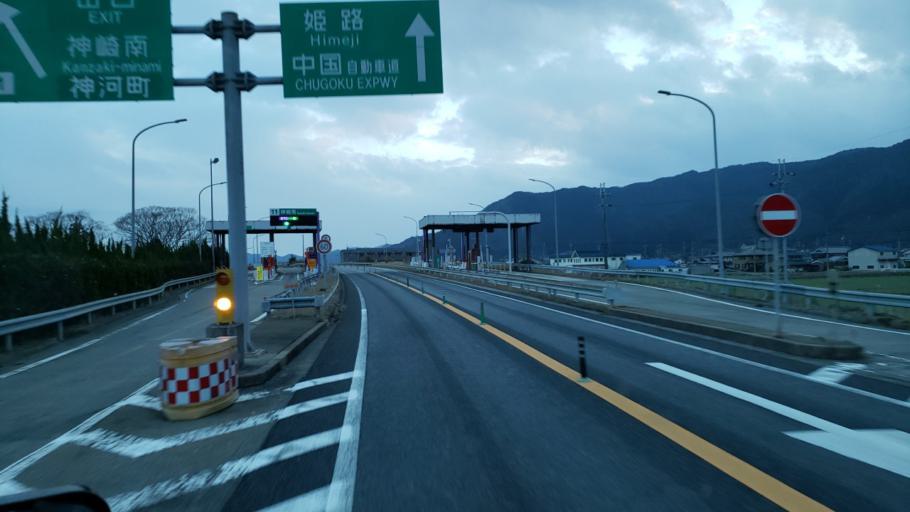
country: JP
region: Hyogo
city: Yamazakicho-nakabirose
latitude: 35.0598
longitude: 134.7644
